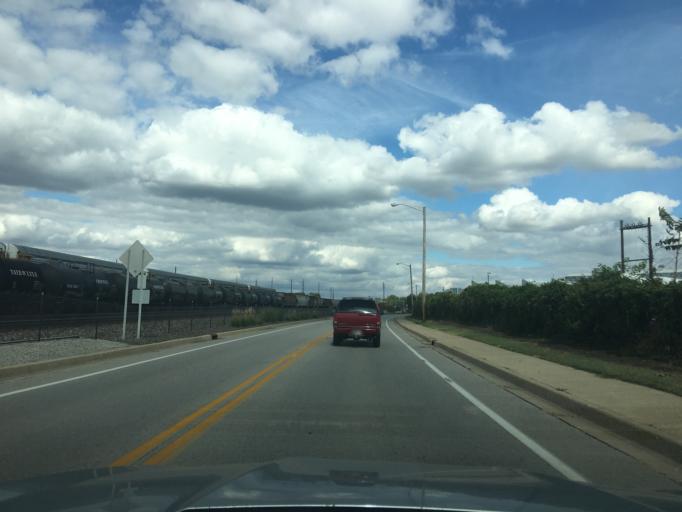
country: US
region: Indiana
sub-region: Tippecanoe County
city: West Lafayette
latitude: 40.4292
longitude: -86.8905
